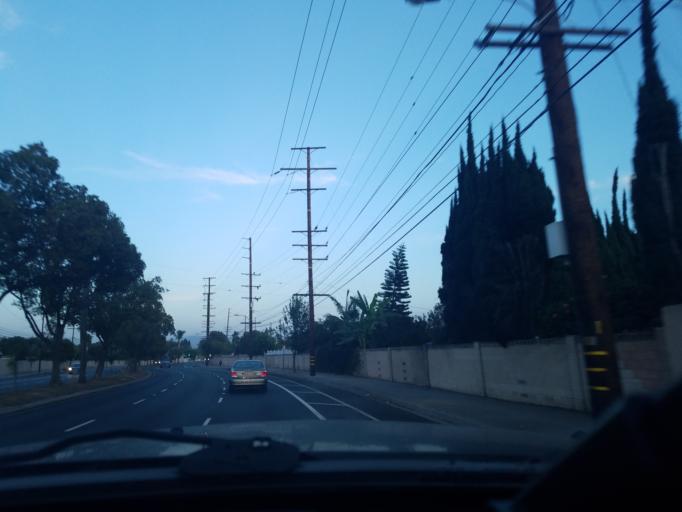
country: US
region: California
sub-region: Orange County
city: Santa Ana
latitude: 33.7155
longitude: -117.8930
